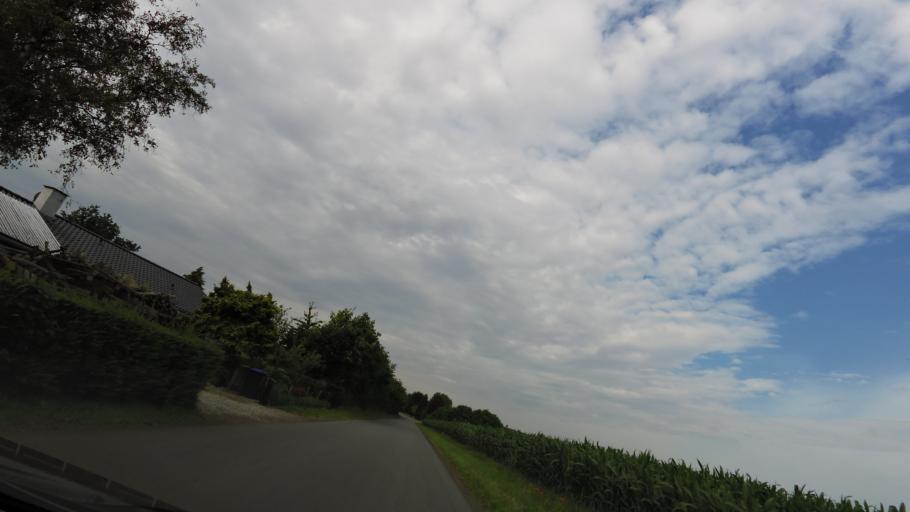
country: DK
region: South Denmark
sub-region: Nordfyns Kommune
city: Otterup
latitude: 55.5570
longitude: 10.4113
